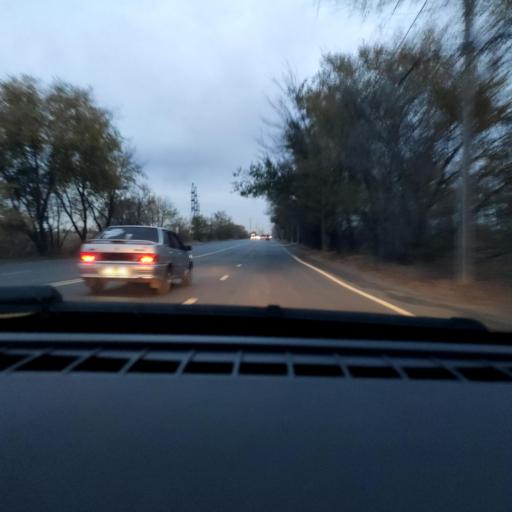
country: RU
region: Voronezj
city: Maslovka
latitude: 51.6257
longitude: 39.2824
